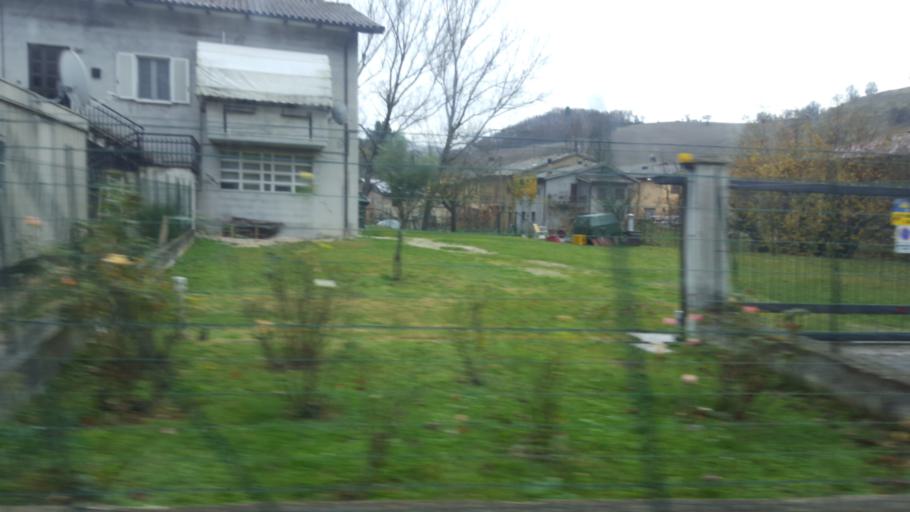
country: IT
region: The Marches
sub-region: Provincia di Macerata
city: Muccia
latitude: 43.0757
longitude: 13.0569
